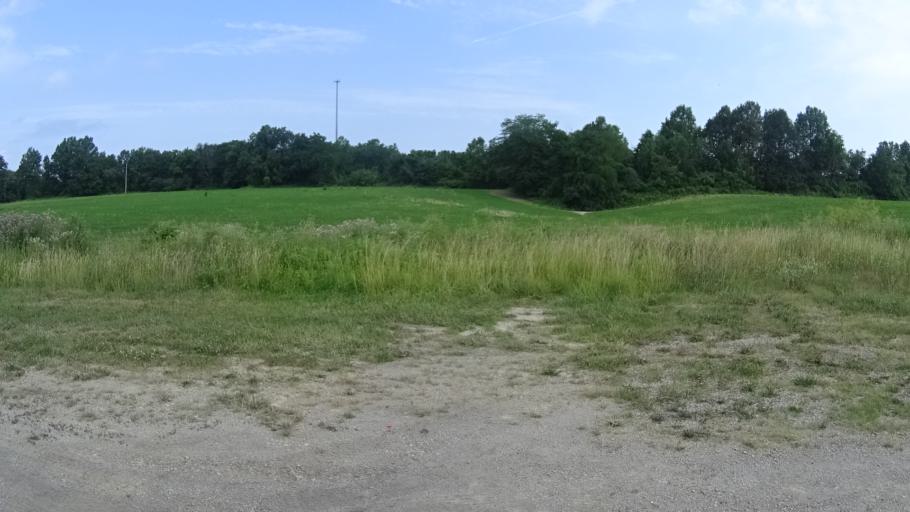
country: US
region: Ohio
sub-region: Lorain County
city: Vermilion
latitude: 41.3828
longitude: -82.4284
